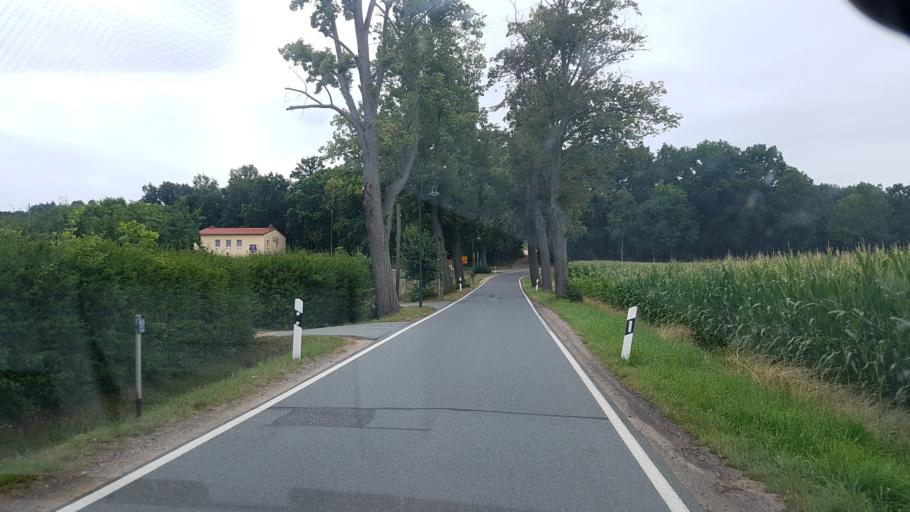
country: DE
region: Saxony
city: Kodersdorf
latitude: 51.2255
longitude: 14.8541
